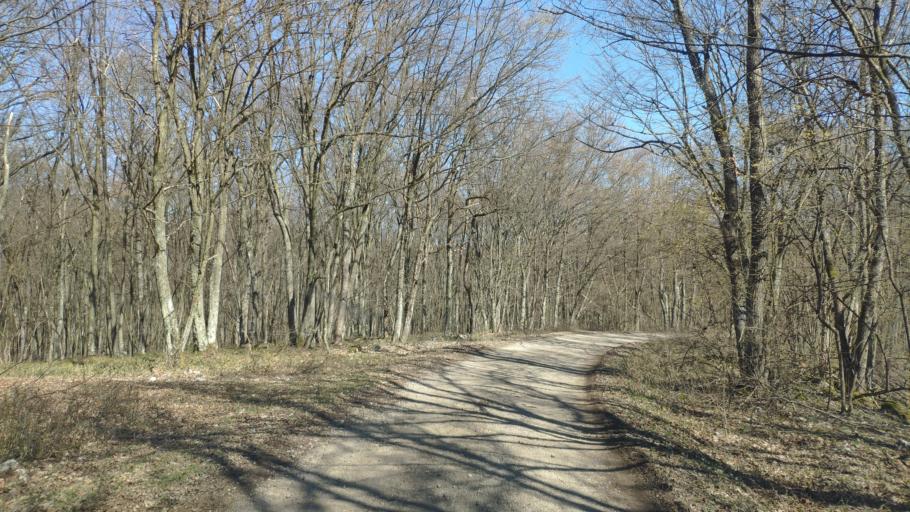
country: SK
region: Kosicky
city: Roznava
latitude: 48.5939
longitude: 20.4094
